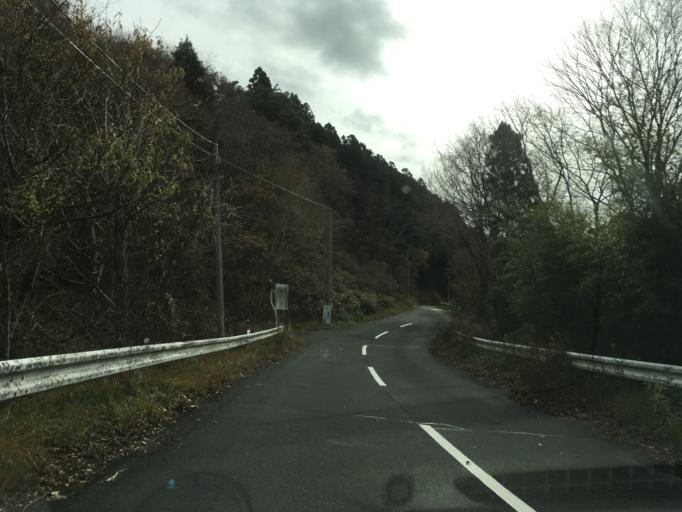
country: JP
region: Iwate
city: Ichinoseki
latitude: 38.7876
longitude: 141.2646
